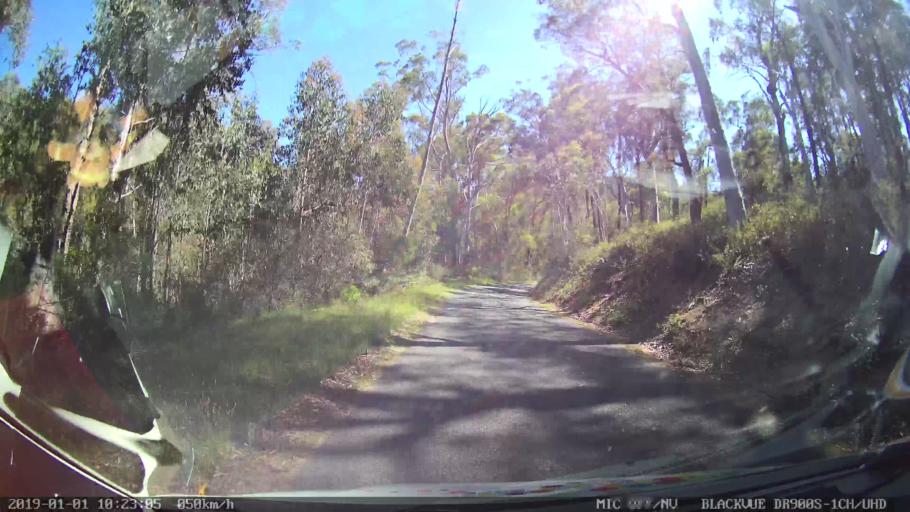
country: AU
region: New South Wales
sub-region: Snowy River
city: Jindabyne
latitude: -36.0760
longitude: 148.2091
